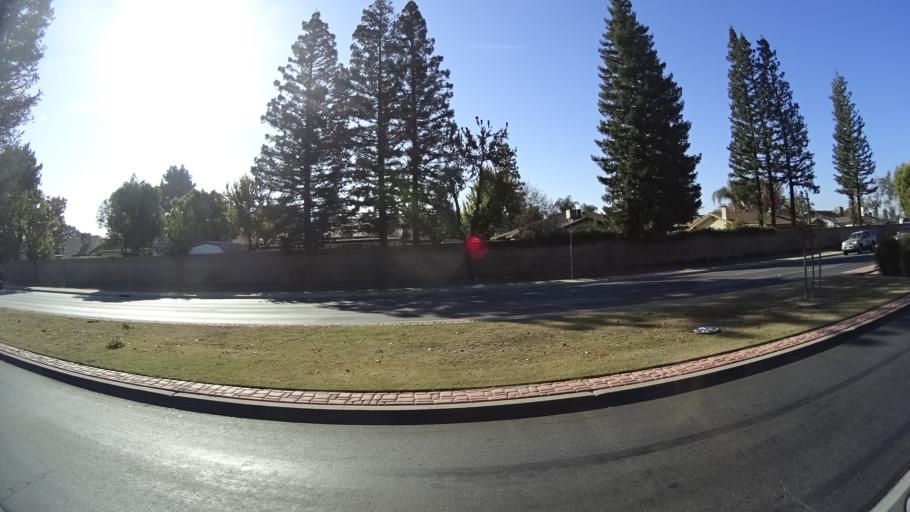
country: US
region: California
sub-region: Kern County
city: Greenacres
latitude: 35.3252
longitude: -119.1075
